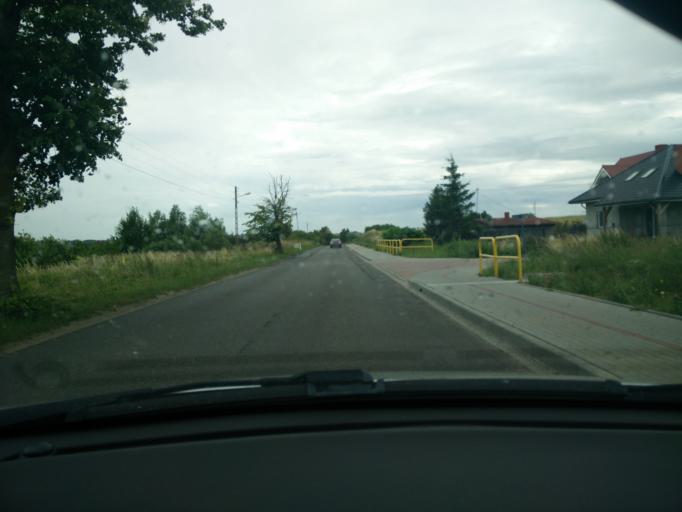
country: PL
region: Pomeranian Voivodeship
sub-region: Powiat pucki
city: Mosty
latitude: 54.6176
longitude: 18.4962
